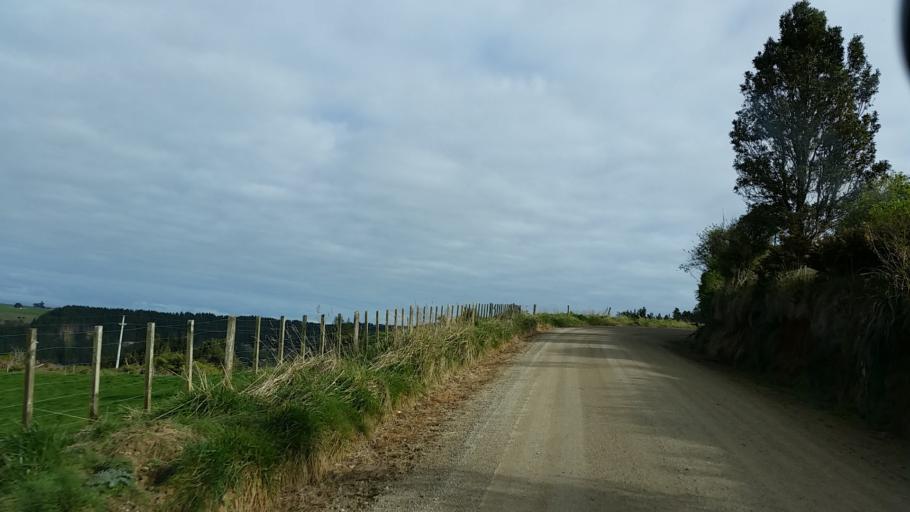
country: NZ
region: Taranaki
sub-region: South Taranaki District
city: Patea
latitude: -39.6906
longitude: 174.6588
